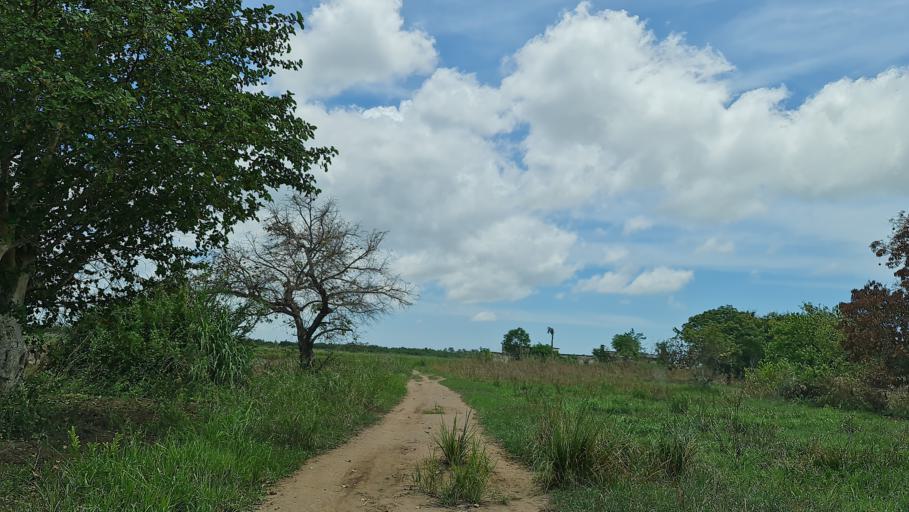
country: MZ
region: Zambezia
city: Quelimane
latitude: -17.5857
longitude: 37.3928
